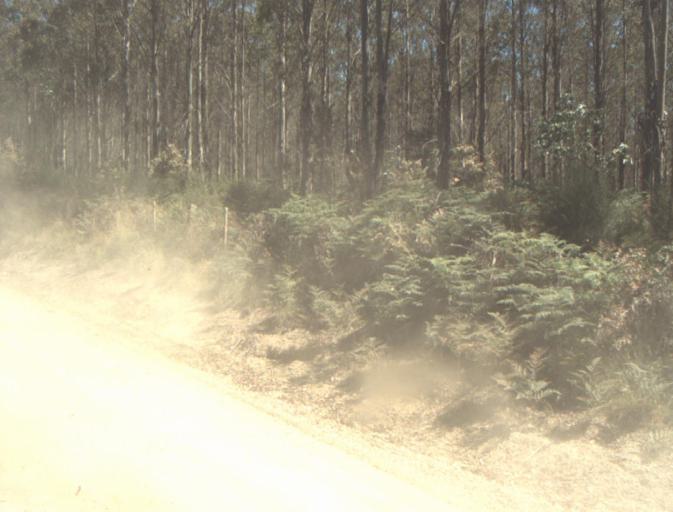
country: AU
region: Tasmania
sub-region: Dorset
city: Scottsdale
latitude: -41.3226
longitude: 147.4459
